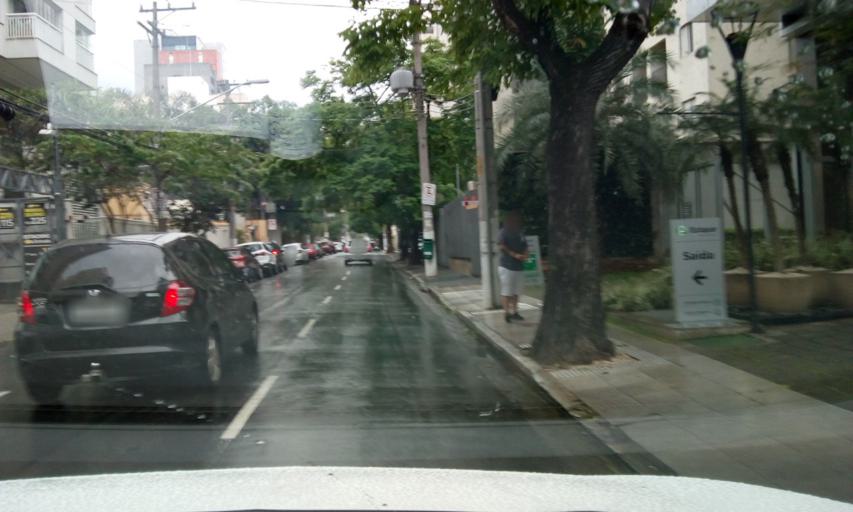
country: BR
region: Sao Paulo
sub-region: Sao Paulo
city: Sao Paulo
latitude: -23.5973
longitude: -46.6822
